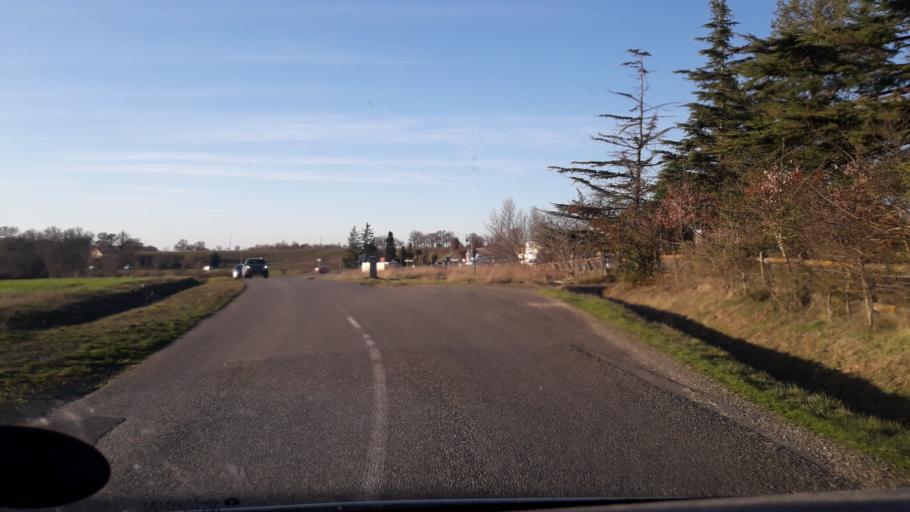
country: FR
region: Midi-Pyrenees
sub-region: Departement du Gers
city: Gimont
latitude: 43.6061
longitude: 0.9780
